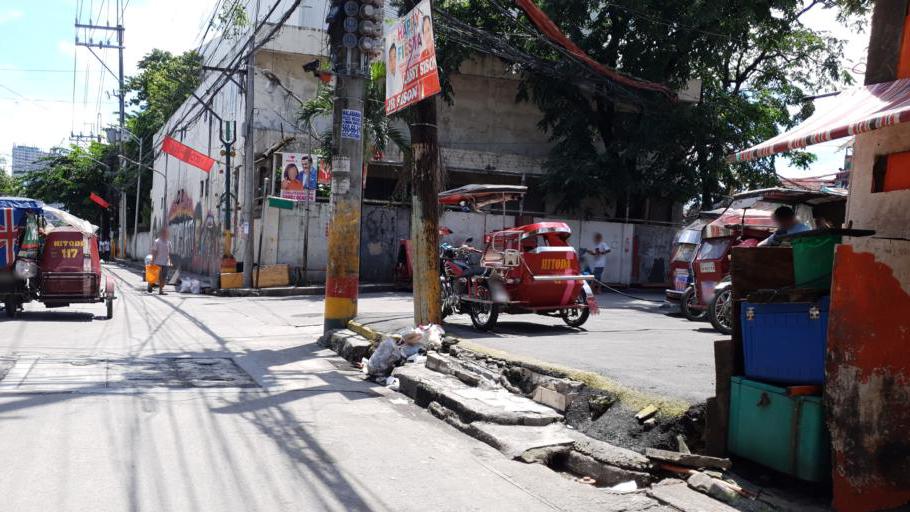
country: PH
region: Metro Manila
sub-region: City of Manila
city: Quiapo
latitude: 14.5988
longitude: 121.0059
